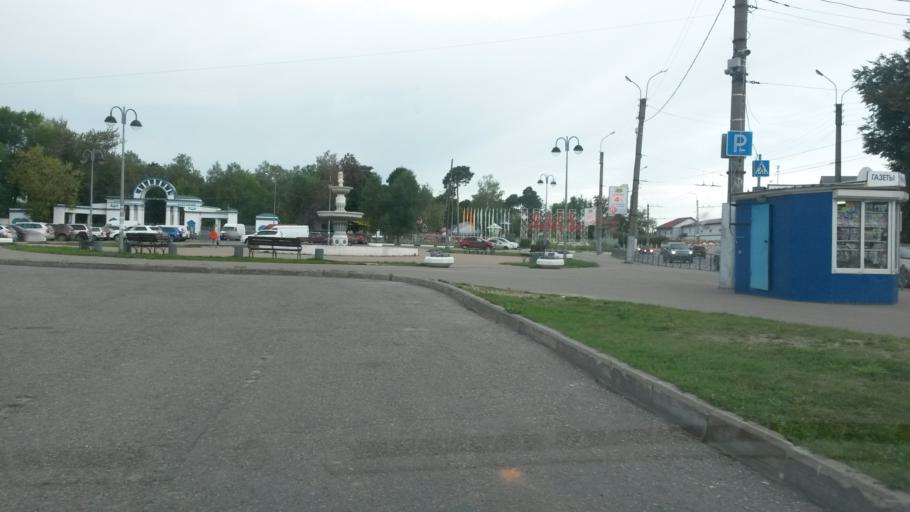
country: RU
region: Ivanovo
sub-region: Gorod Ivanovo
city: Ivanovo
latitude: 57.0208
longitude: 40.9515
